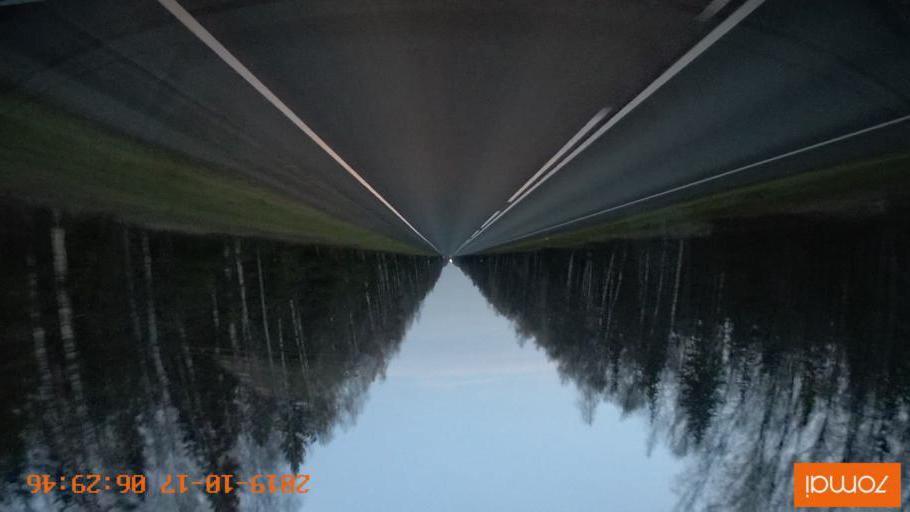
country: RU
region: Ivanovo
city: Lezhnevo
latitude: 56.7423
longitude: 40.7361
